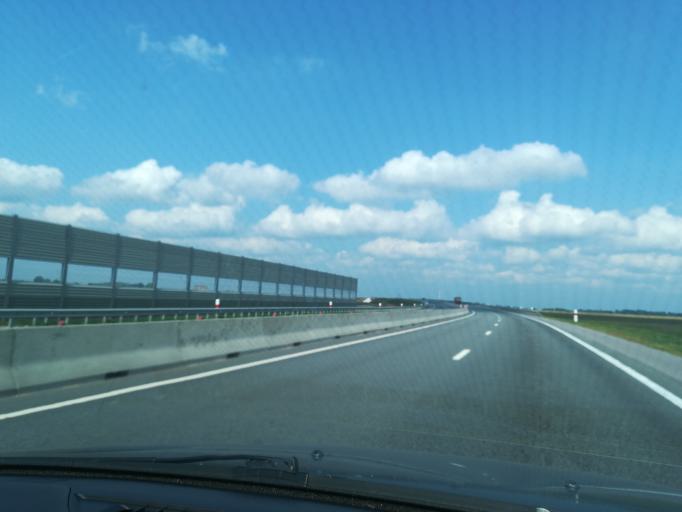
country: RU
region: Leningrad
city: Kingisepp
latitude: 59.5798
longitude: 28.7701
